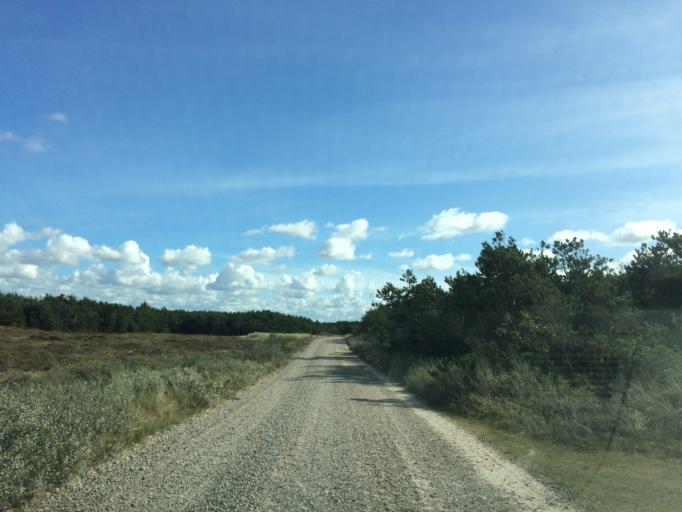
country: DK
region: Central Jutland
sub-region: Holstebro Kommune
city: Ulfborg
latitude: 56.2889
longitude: 8.1339
